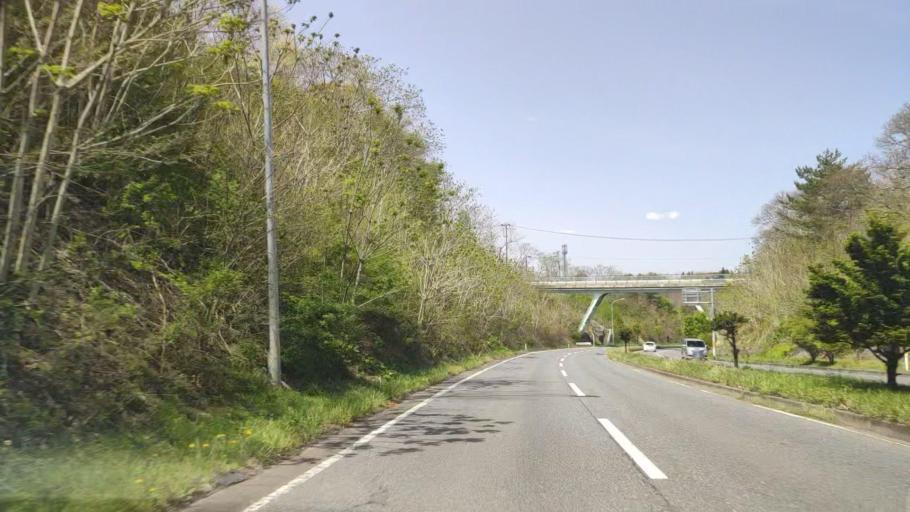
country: JP
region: Aomori
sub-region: Hachinohe Shi
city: Uchimaru
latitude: 40.4959
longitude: 141.4601
